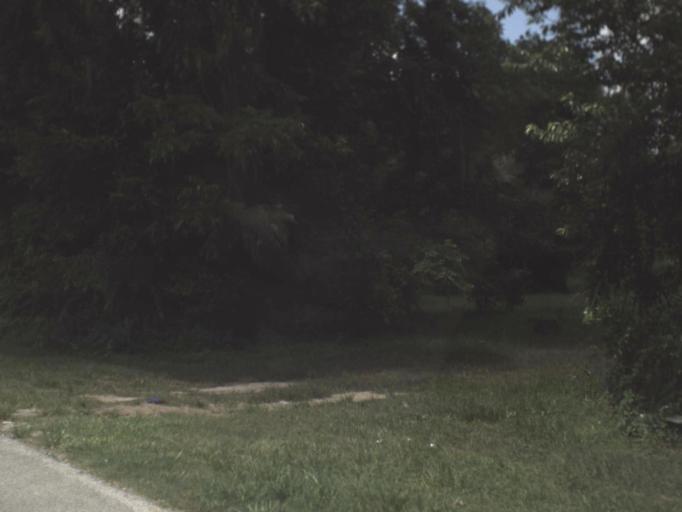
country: US
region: Florida
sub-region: Gilchrist County
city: Trenton
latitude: 29.6069
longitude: -82.8183
